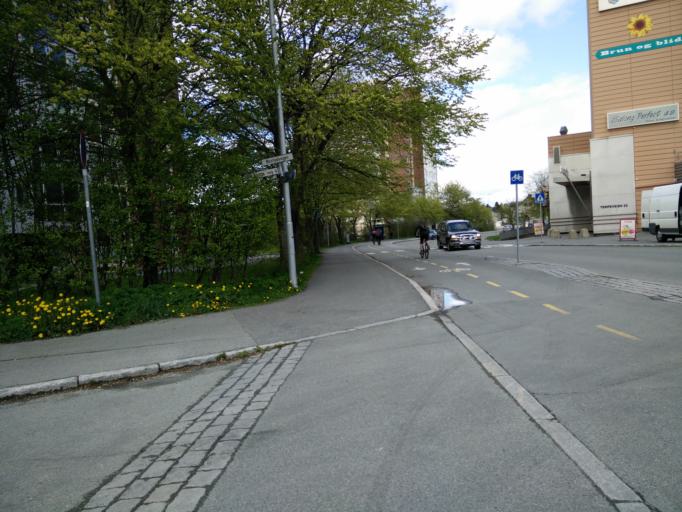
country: NO
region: Sor-Trondelag
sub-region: Trondheim
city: Trondheim
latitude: 63.4070
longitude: 10.3970
